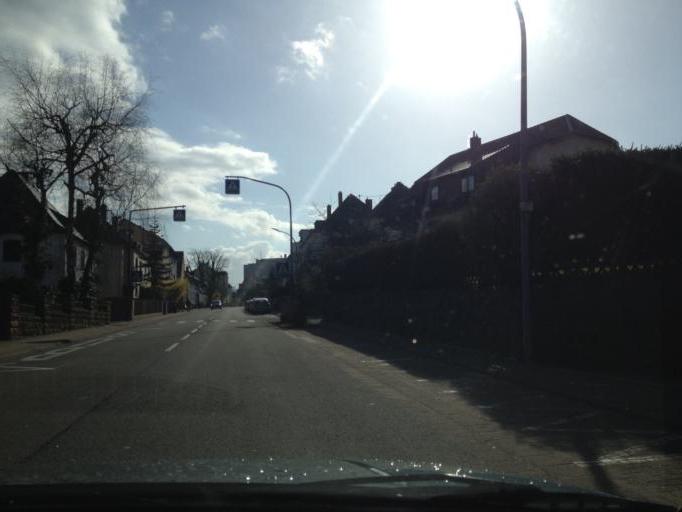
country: DE
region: Saarland
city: Neunkirchen
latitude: 49.3441
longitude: 7.1876
